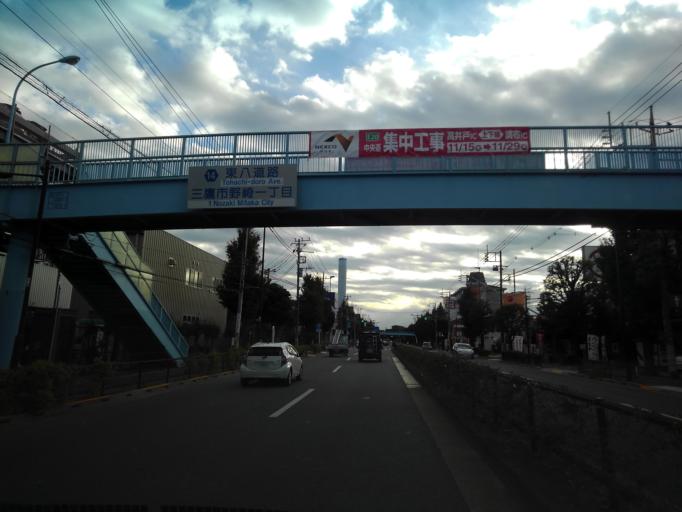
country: JP
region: Tokyo
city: Mitaka-shi
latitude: 35.6815
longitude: 139.5535
